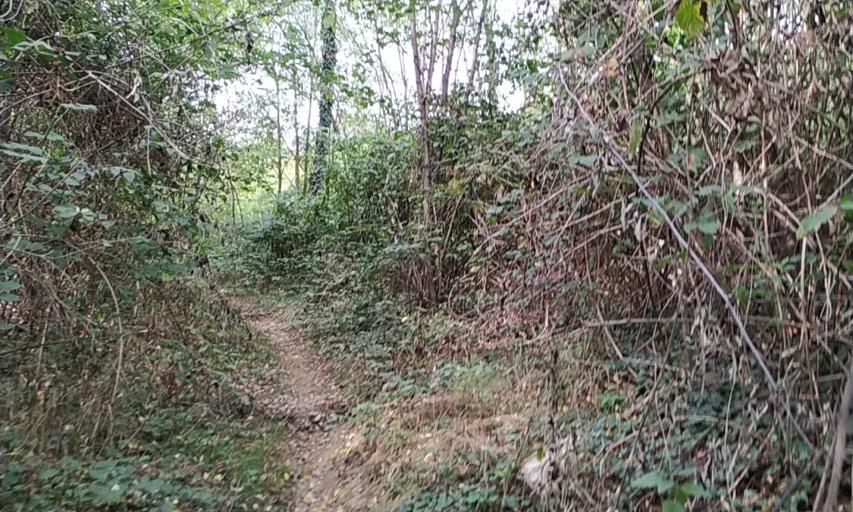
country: IT
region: Piedmont
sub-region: Provincia di Biella
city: Dorzano
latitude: 45.4292
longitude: 8.0924
